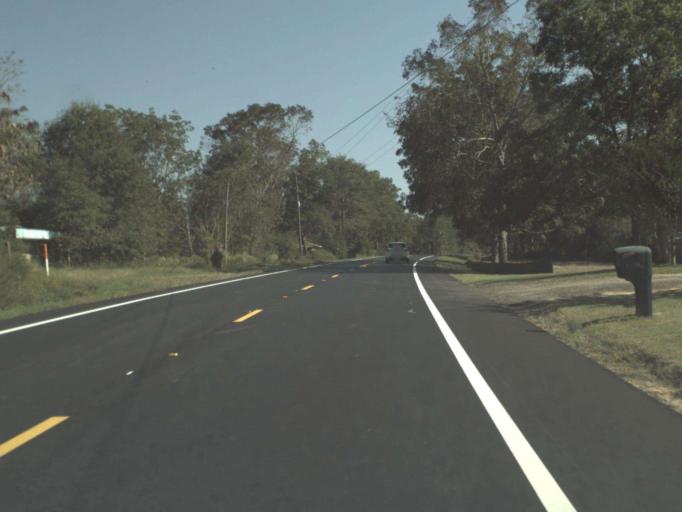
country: US
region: Alabama
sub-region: Covington County
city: Florala
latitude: 30.9499
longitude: -86.2876
